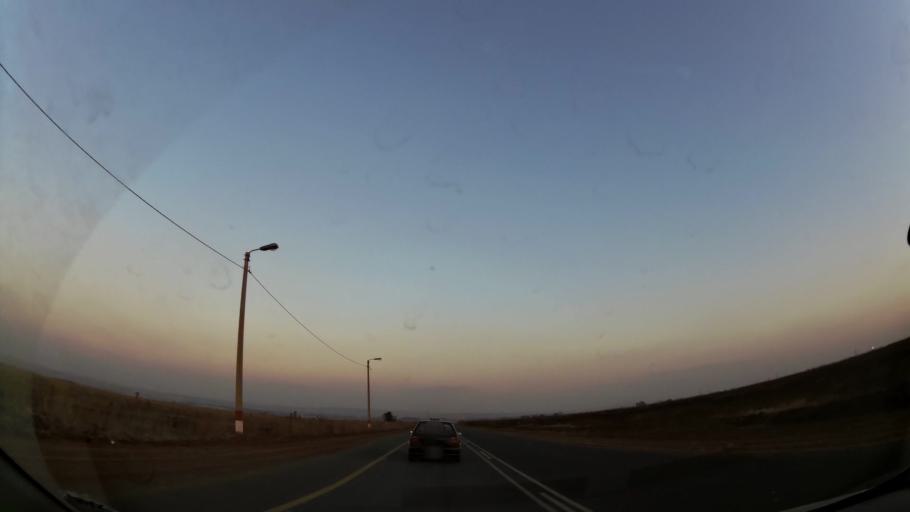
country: ZA
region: Gauteng
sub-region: Ekurhuleni Metropolitan Municipality
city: Nigel
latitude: -26.3647
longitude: 28.4187
